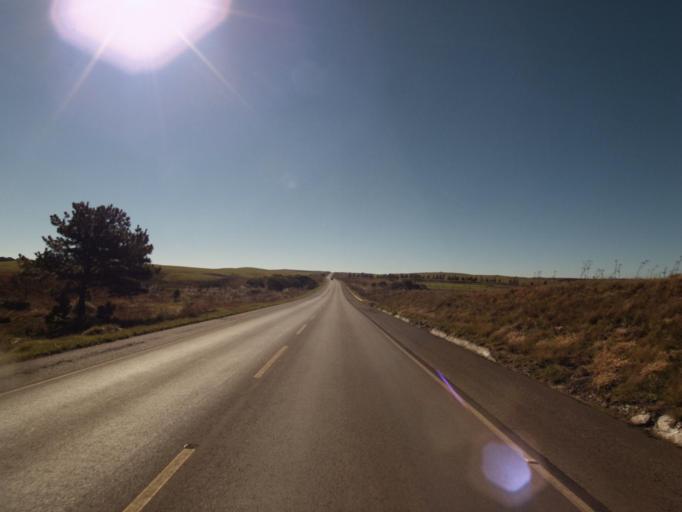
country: BR
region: Parana
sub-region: Palmas
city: Palmas
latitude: -26.7276
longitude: -51.6371
